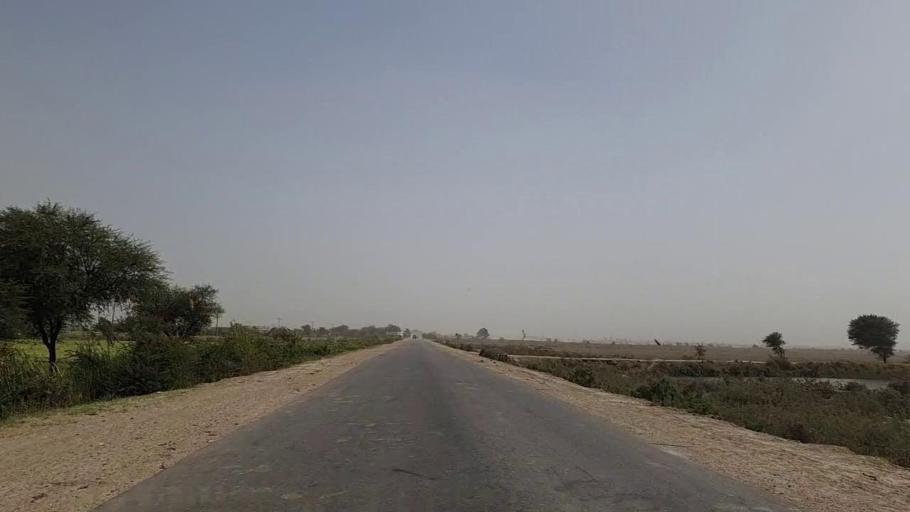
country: PK
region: Sindh
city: Talhar
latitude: 24.8787
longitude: 68.8331
